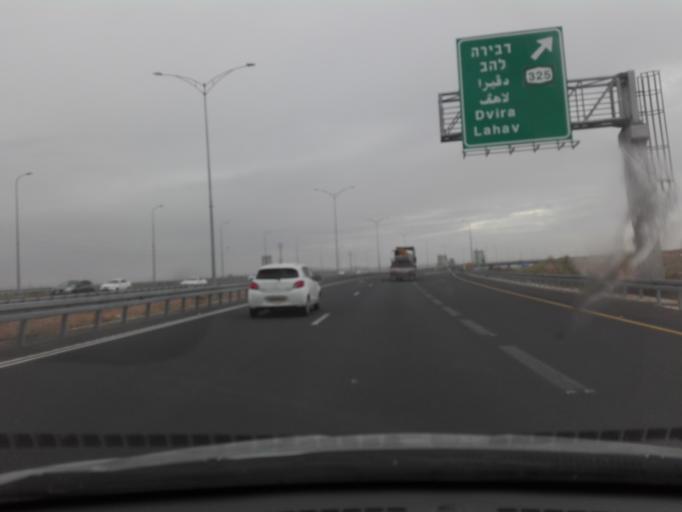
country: IL
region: Southern District
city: Lehavim
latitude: 31.4279
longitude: 34.7819
